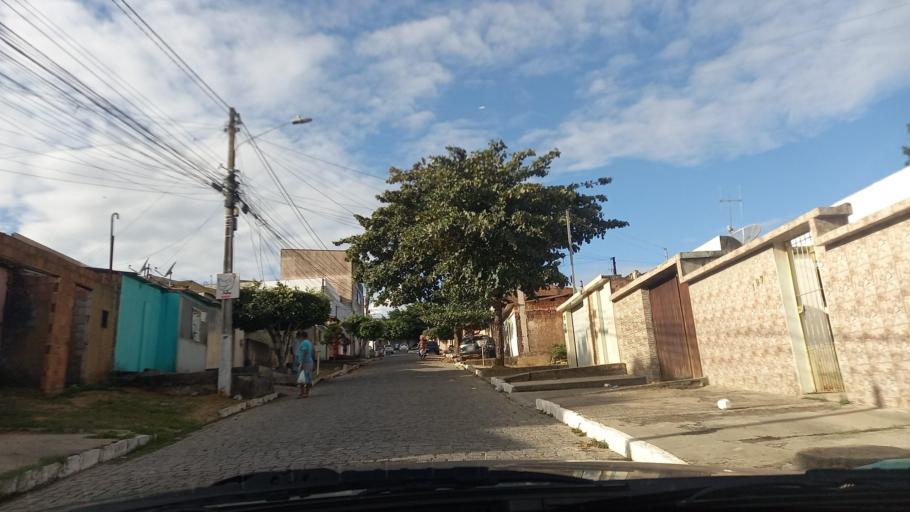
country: BR
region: Pernambuco
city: Garanhuns
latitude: -8.9010
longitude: -36.4967
